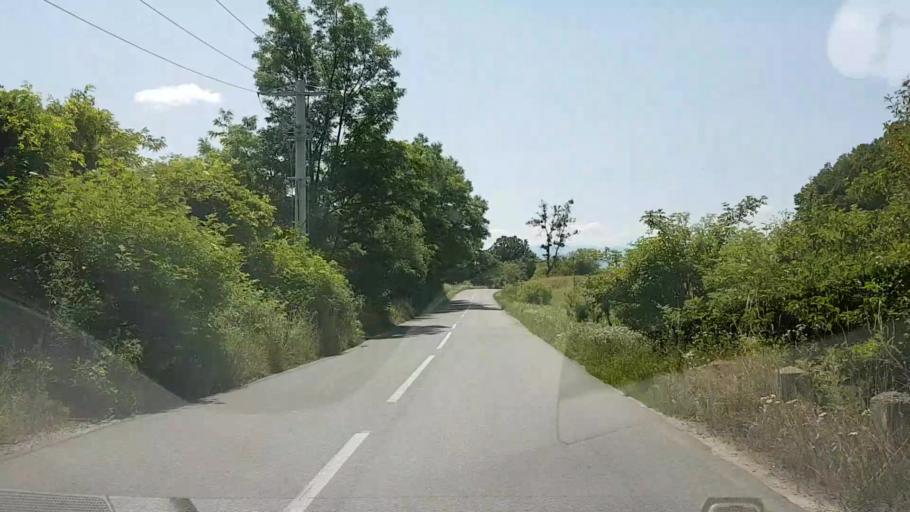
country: RO
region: Brasov
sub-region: Comuna Voila
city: Voila
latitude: 45.8677
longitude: 24.8238
